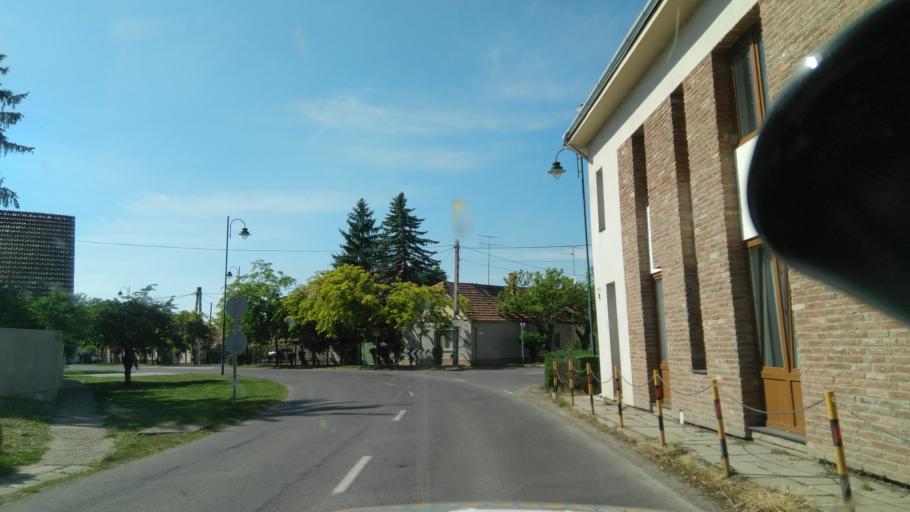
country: HU
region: Bekes
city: Gyula
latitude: 46.6471
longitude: 21.2887
